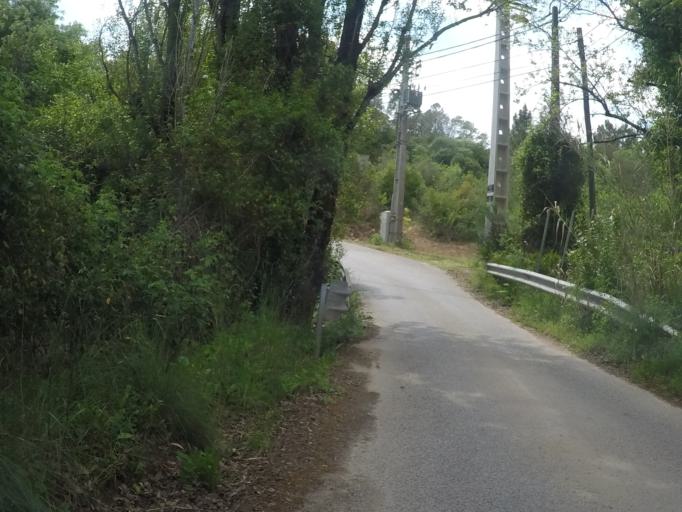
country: PT
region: Setubal
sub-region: Palmela
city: Quinta do Anjo
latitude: 38.4997
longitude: -8.9985
